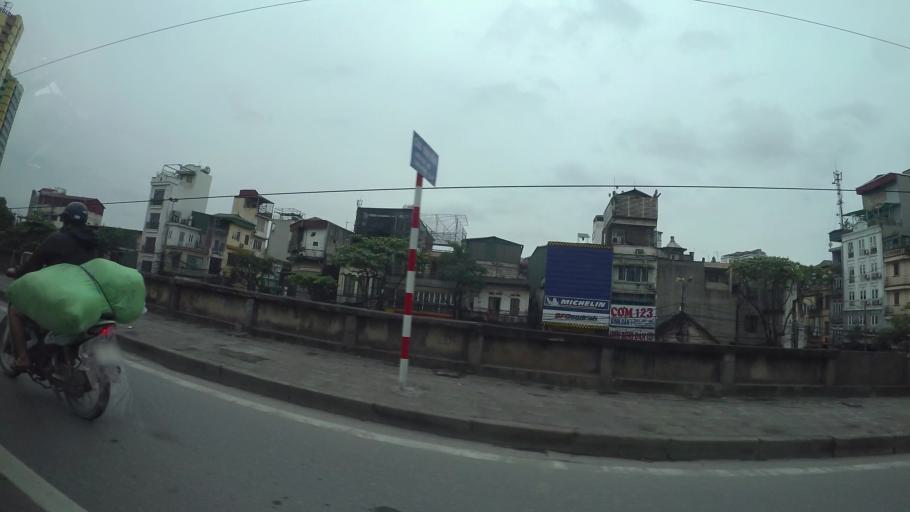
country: VN
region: Ha Noi
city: Hai BaTrung
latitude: 21.0138
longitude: 105.8632
